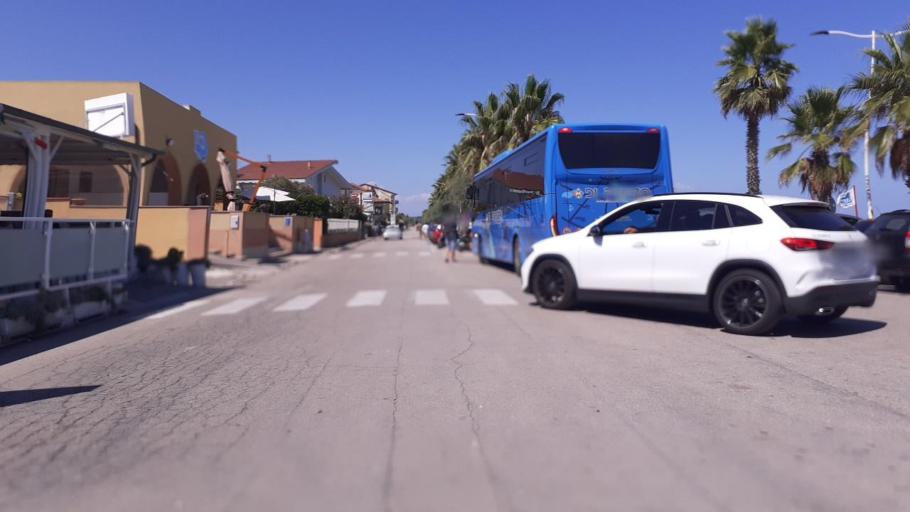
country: IT
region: Abruzzo
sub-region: Provincia di Chieti
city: Casalbordino-Miracoli
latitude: 42.1945
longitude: 14.6344
